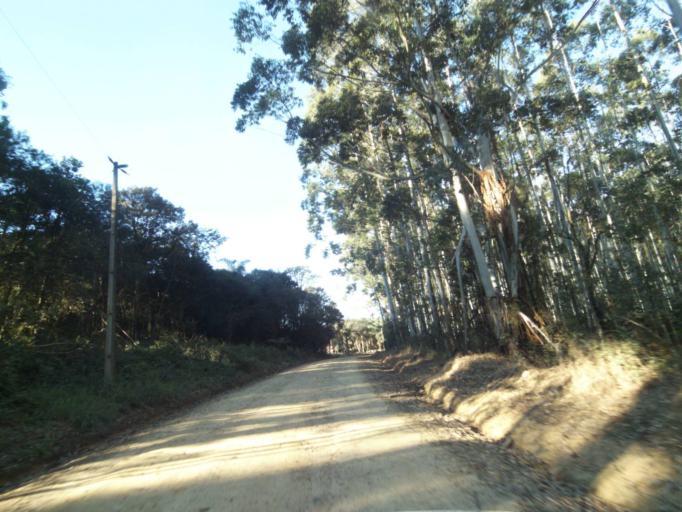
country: BR
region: Parana
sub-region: Telemaco Borba
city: Telemaco Borba
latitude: -24.5115
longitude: -50.6586
